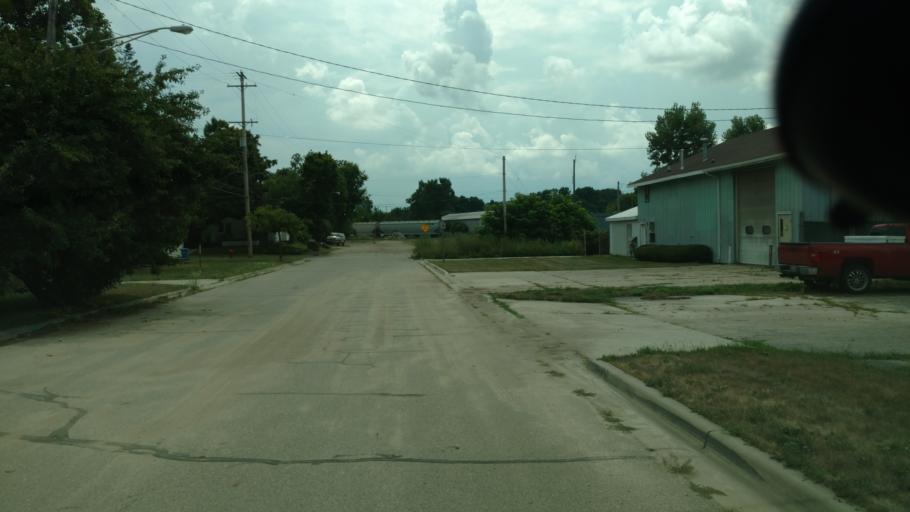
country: US
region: Michigan
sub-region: Ingham County
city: Lansing
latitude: 42.7605
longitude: -84.5589
